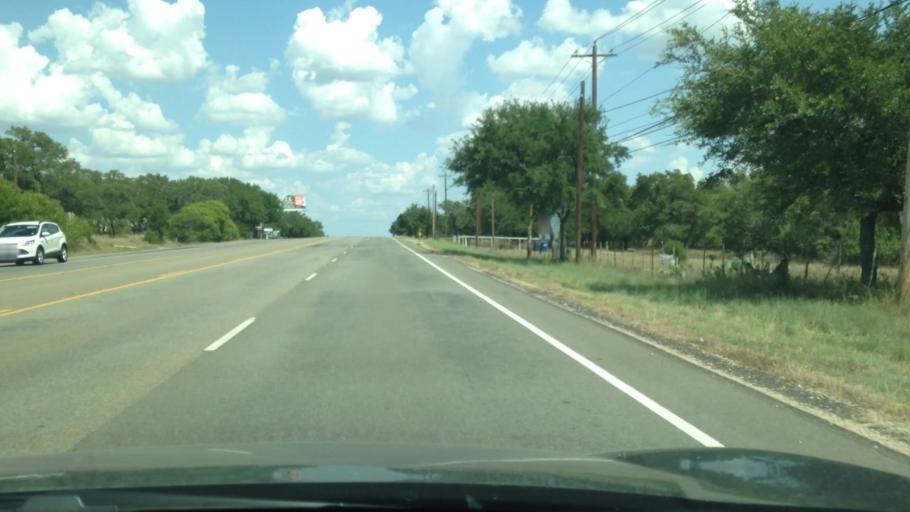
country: US
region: Texas
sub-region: Williamson County
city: Leander
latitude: 30.6341
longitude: -97.7762
